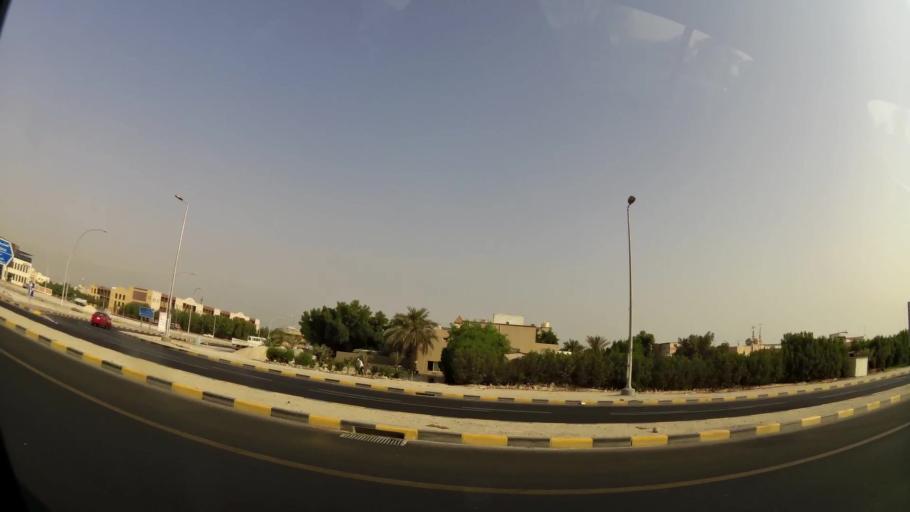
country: KW
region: Al Asimah
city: Ar Rabiyah
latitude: 29.3112
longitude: 47.8484
